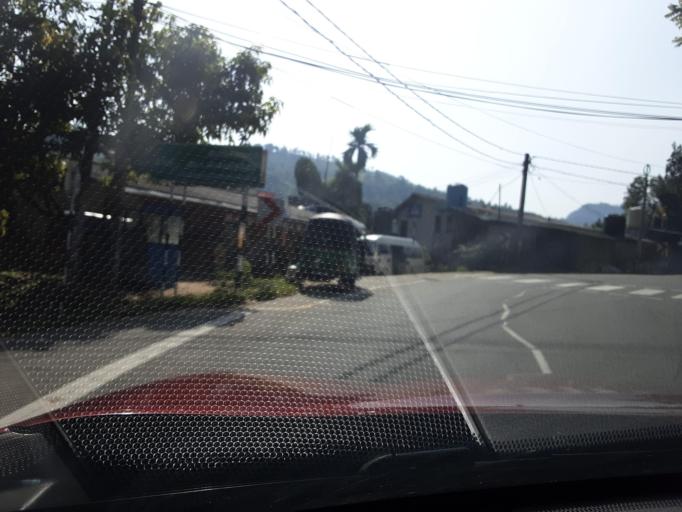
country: LK
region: Uva
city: Badulla
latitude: 6.9858
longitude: 81.0778
